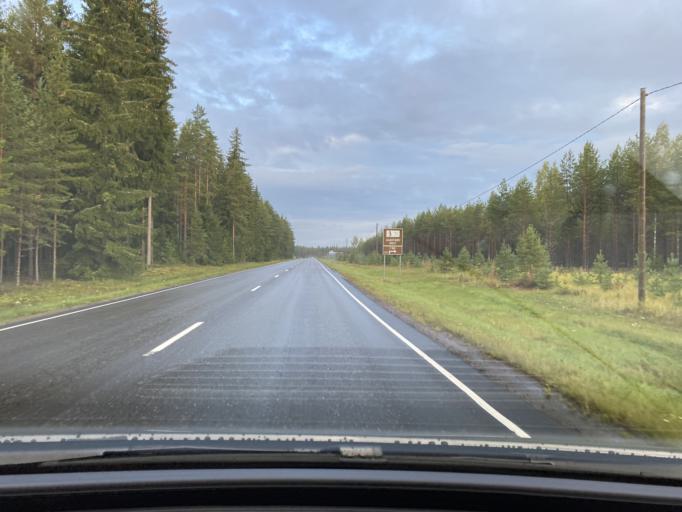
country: FI
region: Satakunta
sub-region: Pori
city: Vampula
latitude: 60.9525
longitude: 22.6717
